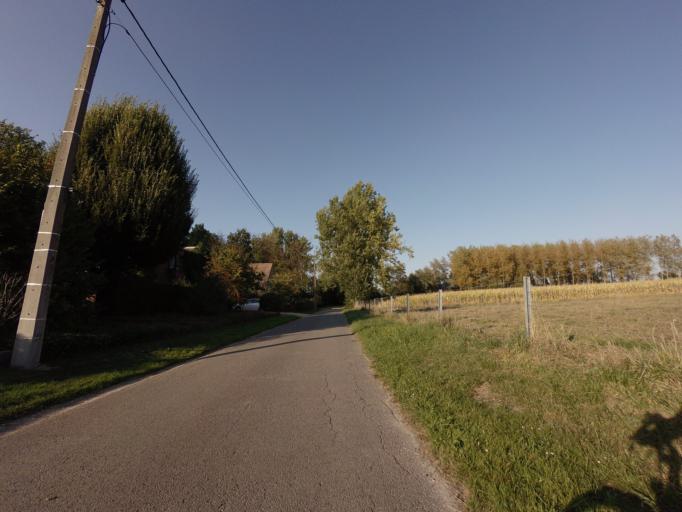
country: BE
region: Flanders
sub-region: Provincie Vlaams-Brabant
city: Haacht
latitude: 50.9355
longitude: 4.6289
